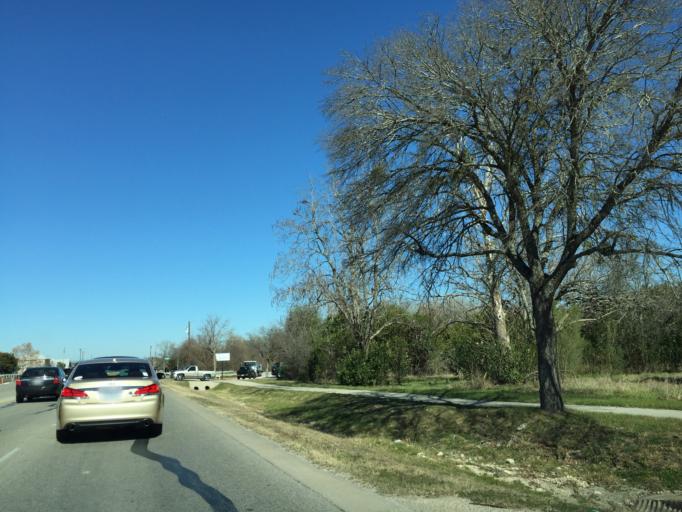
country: US
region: Texas
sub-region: Williamson County
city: Leander
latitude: 30.5541
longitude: -97.8578
